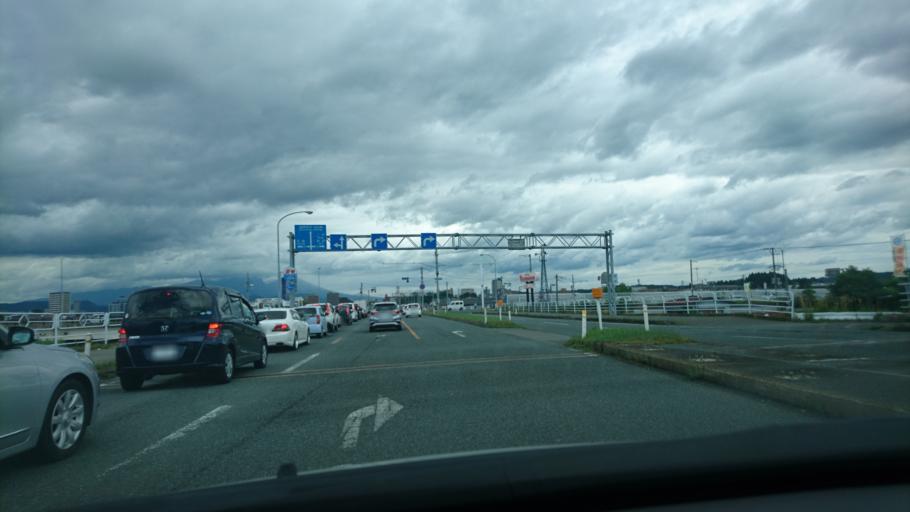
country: JP
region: Iwate
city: Morioka-shi
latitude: 39.6846
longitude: 141.1618
